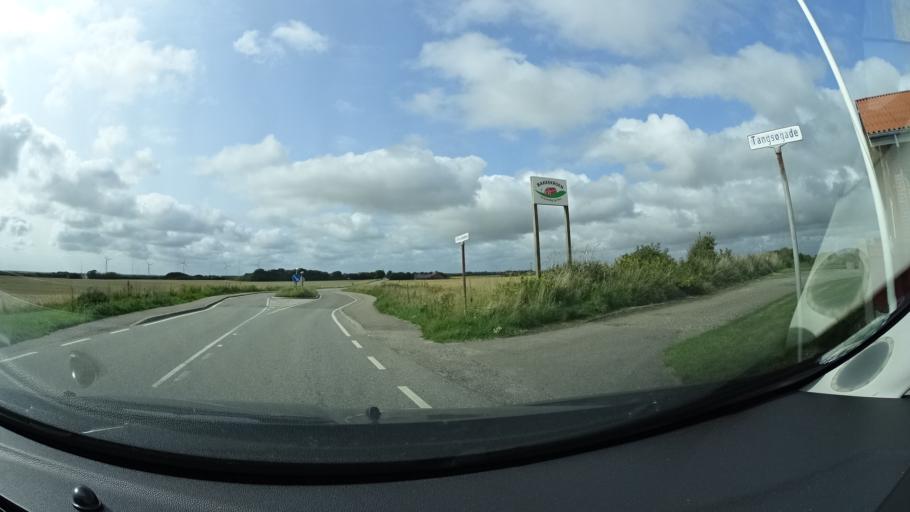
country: DK
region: Central Jutland
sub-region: Lemvig Kommune
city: Lemvig
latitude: 56.4391
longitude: 8.1968
